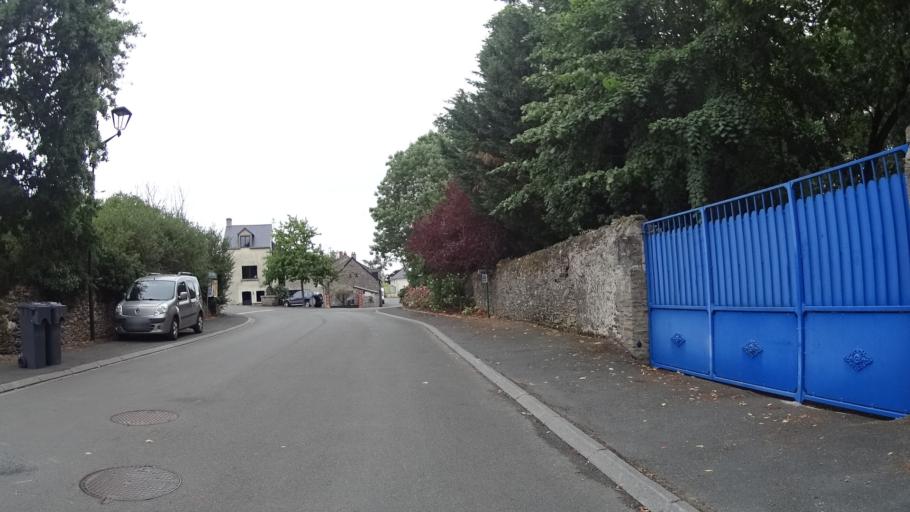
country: FR
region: Pays de la Loire
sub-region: Departement de Maine-et-Loire
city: La Possonniere
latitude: 47.3766
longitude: -0.6831
